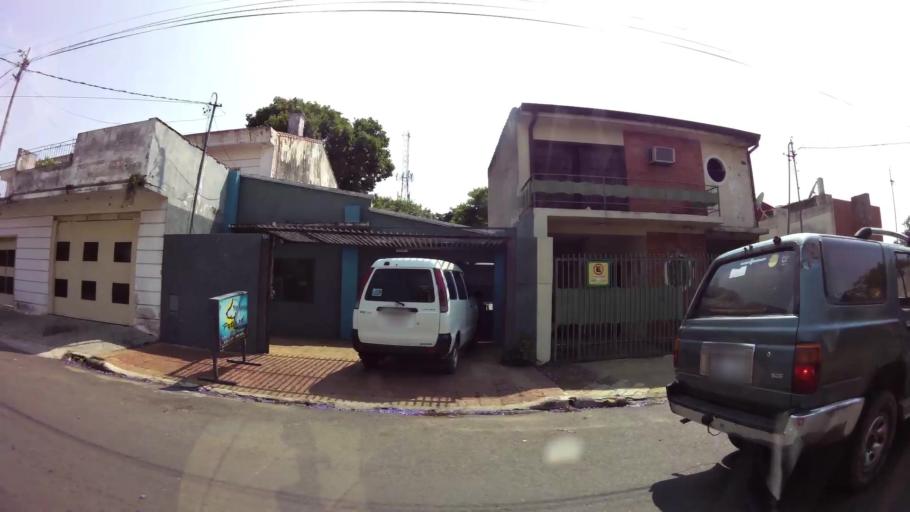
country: PY
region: Asuncion
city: Asuncion
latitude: -25.2890
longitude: -57.6462
